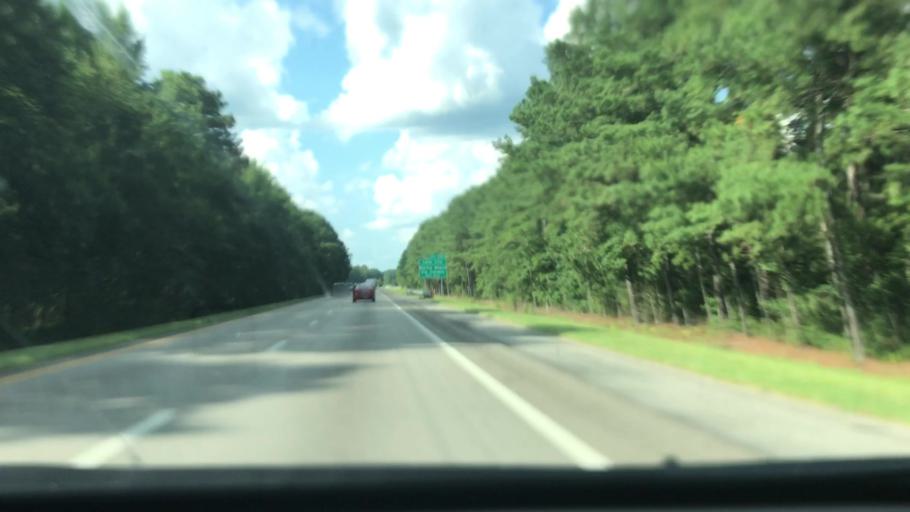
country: US
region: South Carolina
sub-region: Sumter County
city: East Sumter
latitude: 33.8897
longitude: -80.0979
